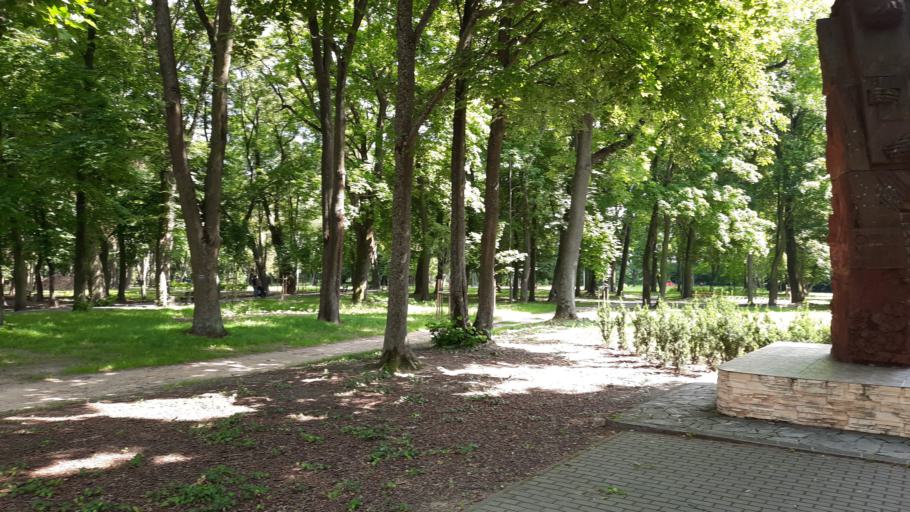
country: PL
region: Masovian Voivodeship
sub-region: Powiat wyszkowski
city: Wyszkow
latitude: 52.5916
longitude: 21.4533
